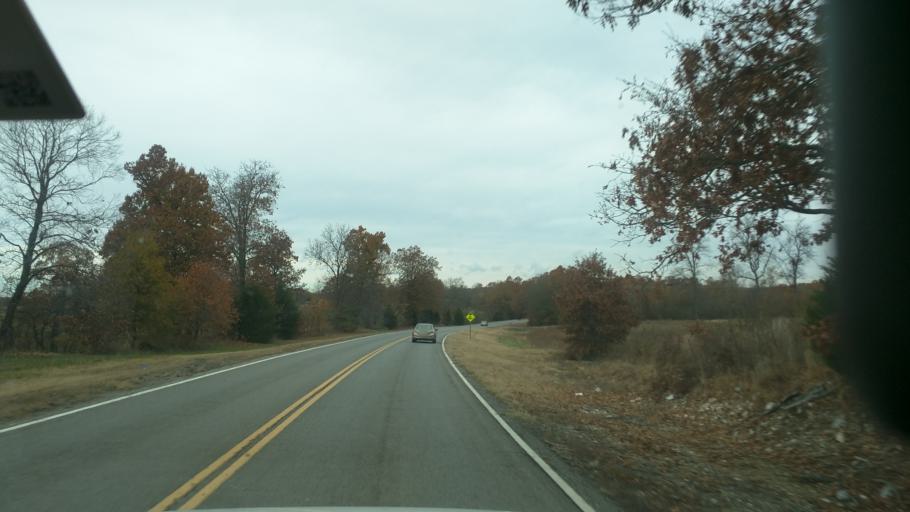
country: US
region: Oklahoma
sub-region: Cherokee County
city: Park Hill
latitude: 35.9046
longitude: -94.8272
